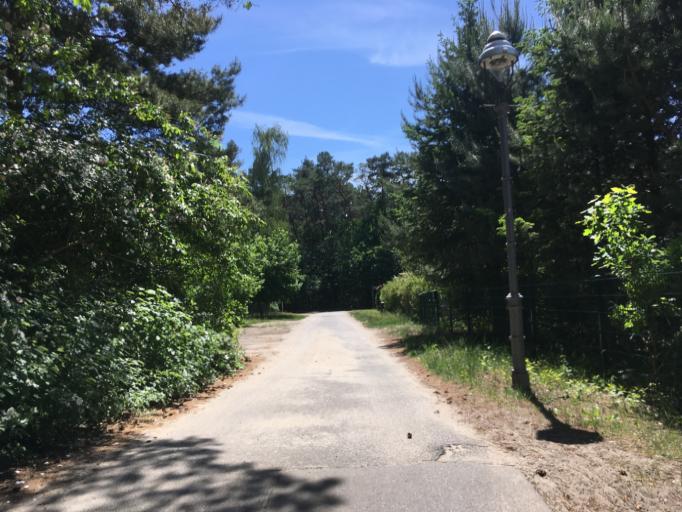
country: DE
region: Berlin
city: Schmockwitz
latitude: 52.3867
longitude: 13.6393
